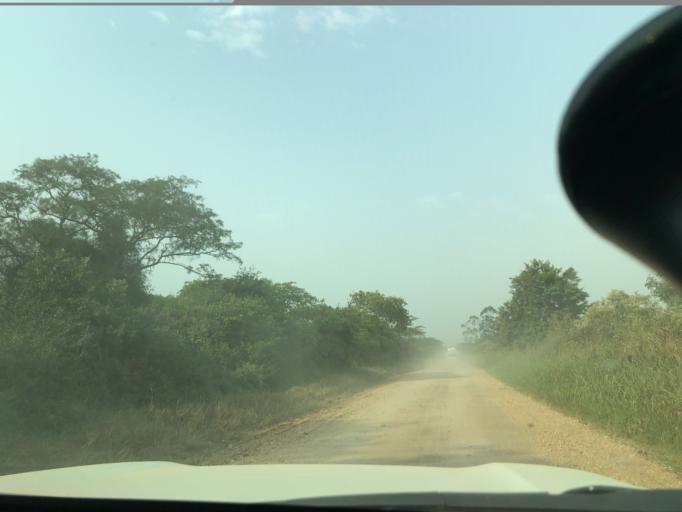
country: CD
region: Nord Kivu
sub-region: North Kivu
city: Butembo
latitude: 0.1613
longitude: 29.6449
